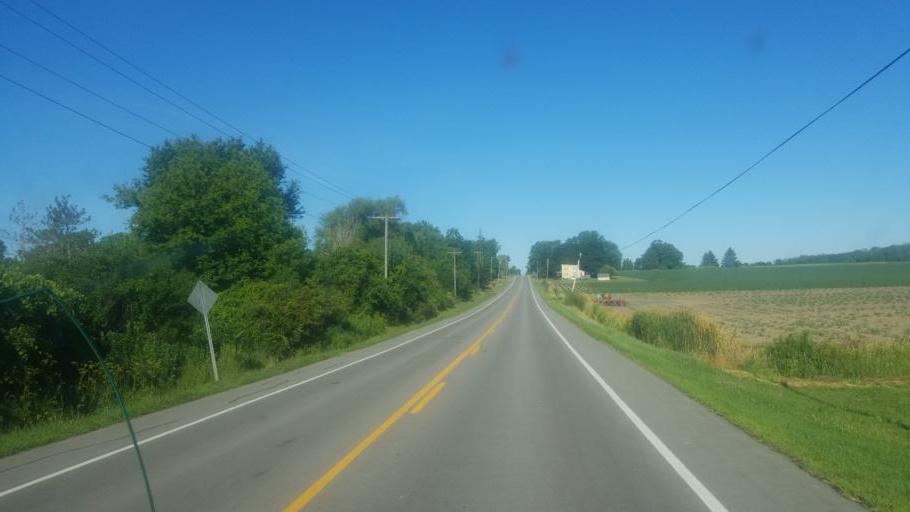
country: US
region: New York
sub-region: Ontario County
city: Phelps
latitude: 42.8865
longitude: -77.0587
